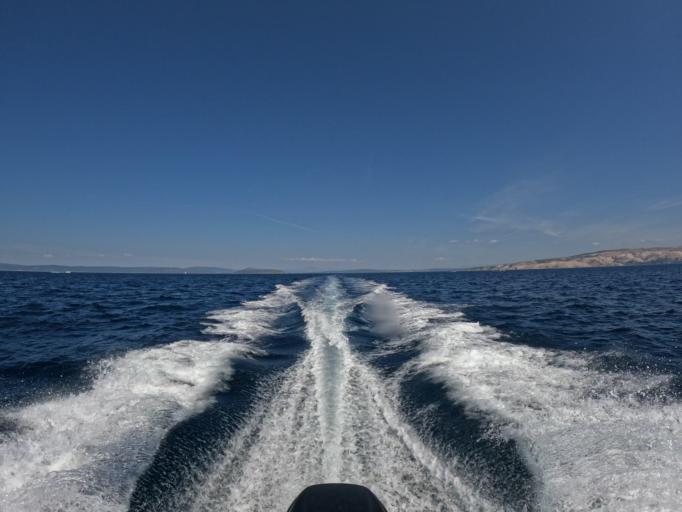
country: HR
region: Primorsko-Goranska
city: Punat
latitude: 44.9016
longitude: 14.6318
